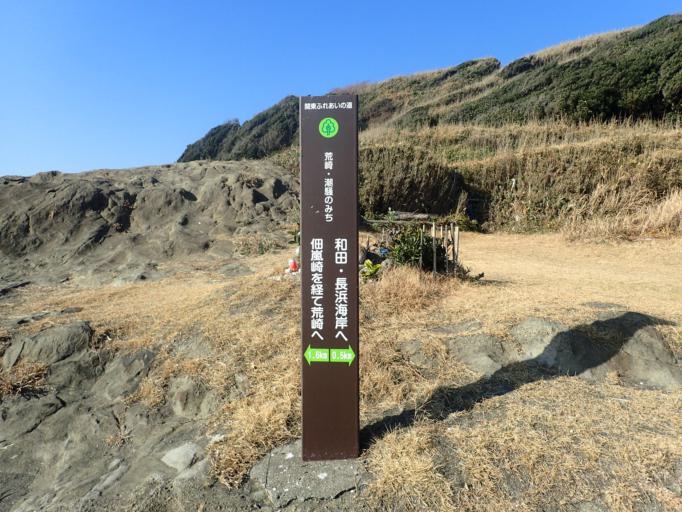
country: JP
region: Kanagawa
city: Miura
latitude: 35.1907
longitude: 139.6105
